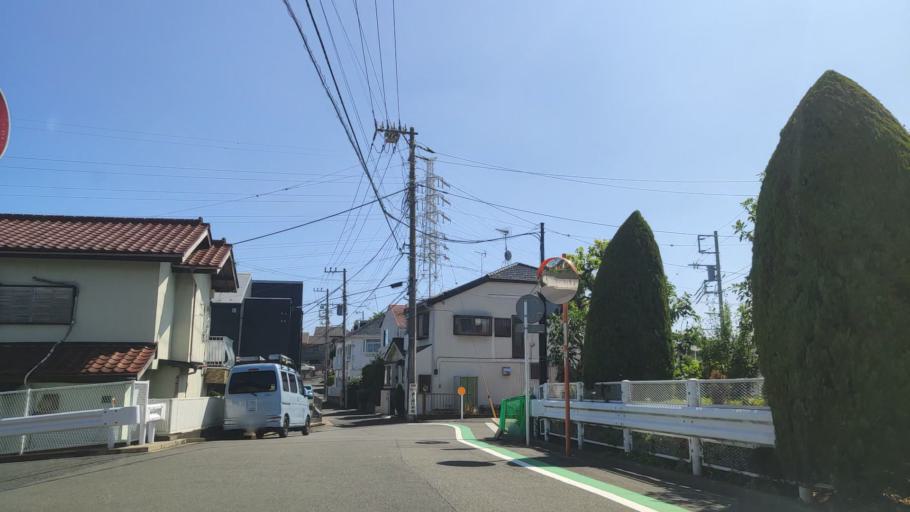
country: JP
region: Kanagawa
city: Yokohama
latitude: 35.5172
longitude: 139.6353
